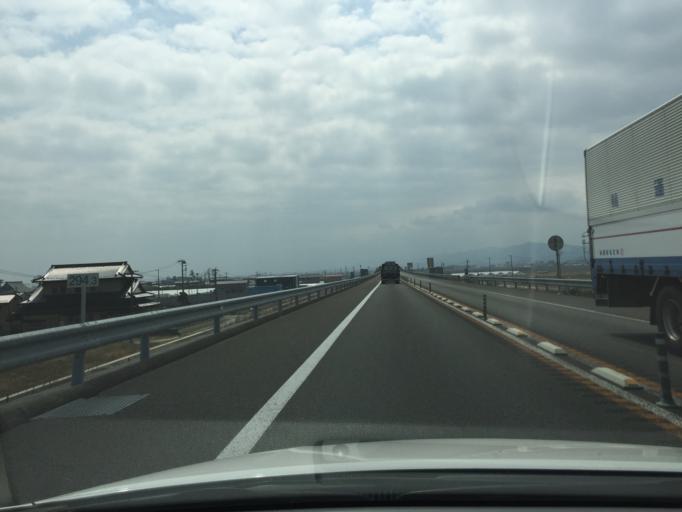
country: JP
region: Miyagi
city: Watari
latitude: 38.0314
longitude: 140.8911
